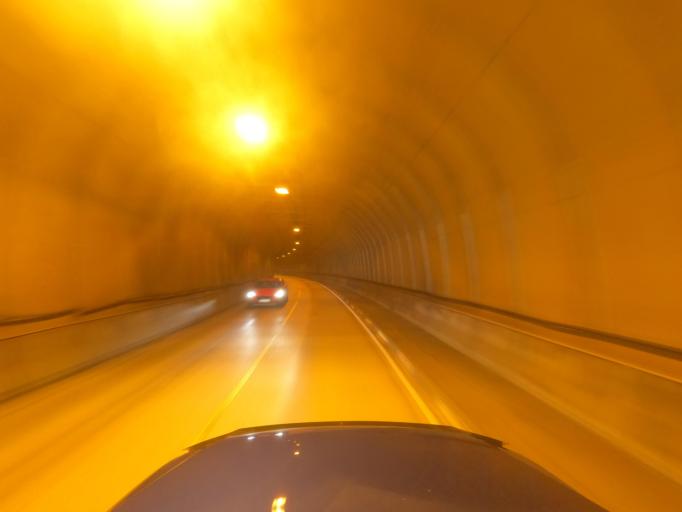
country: NO
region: Nordland
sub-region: Vestvagoy
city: Gravdal
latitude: 68.1494
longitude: 13.4817
